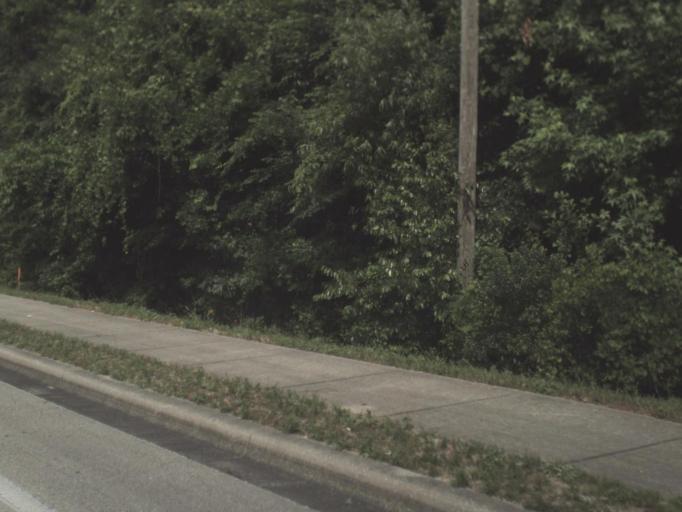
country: US
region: Florida
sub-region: Saint Johns County
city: Saint Augustine South
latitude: 29.8487
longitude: -81.3596
